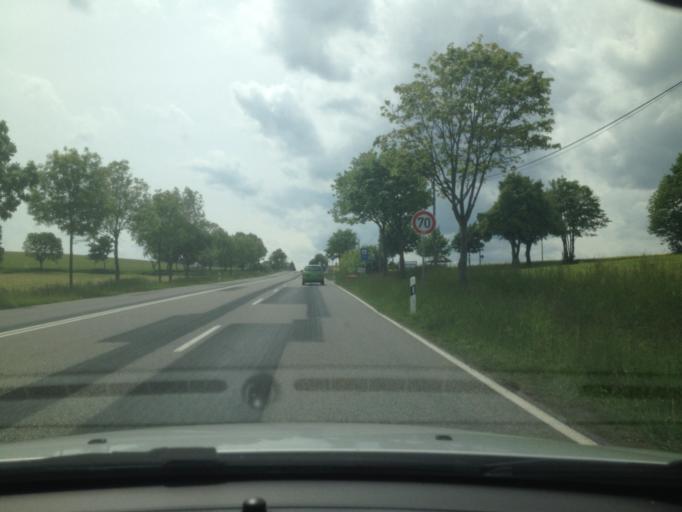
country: DE
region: Saxony
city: Lossnitz
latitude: 50.6630
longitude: 12.7577
